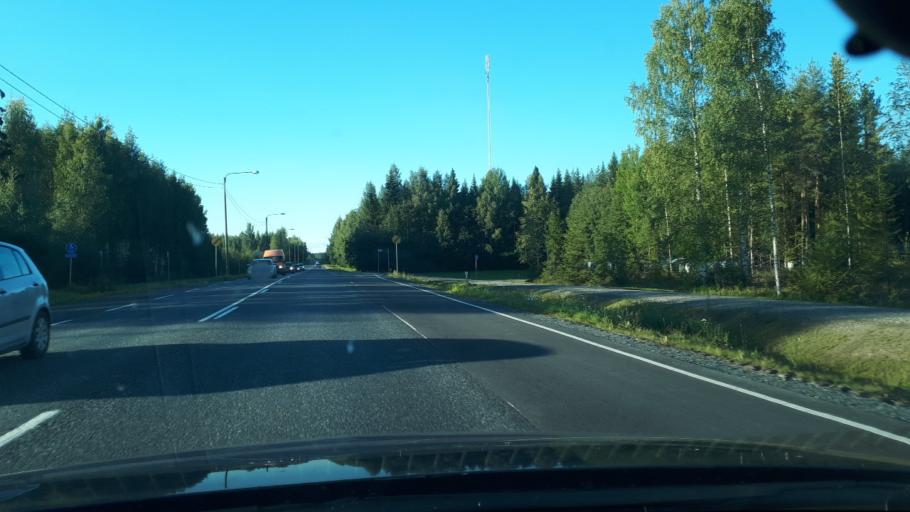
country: FI
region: Northern Savo
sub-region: Ylae-Savo
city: Lapinlahti
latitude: 63.4253
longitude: 27.3297
